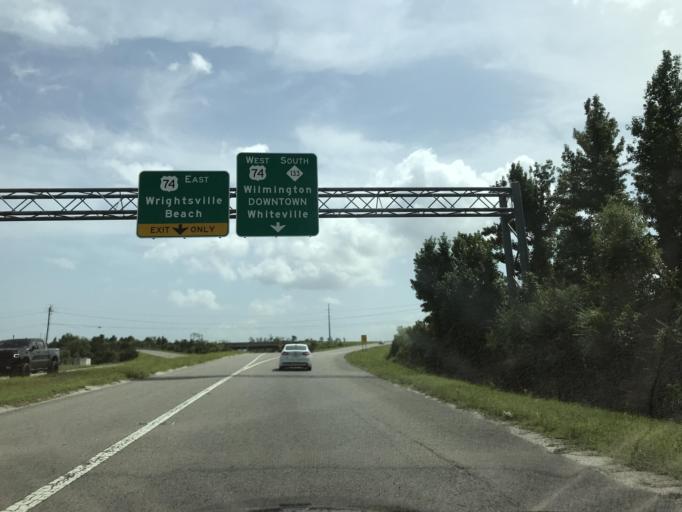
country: US
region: North Carolina
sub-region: New Hanover County
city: Wrightsboro
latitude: 34.2643
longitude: -77.9306
